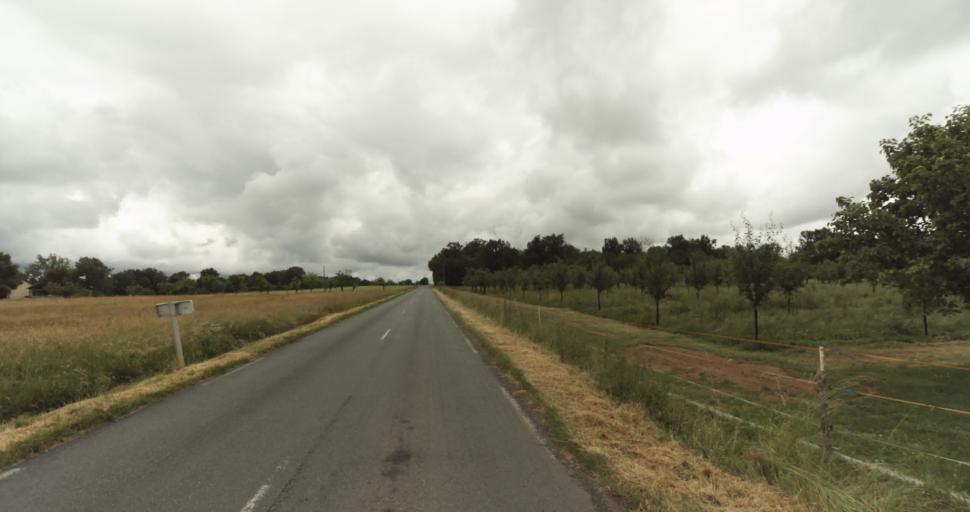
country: FR
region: Aquitaine
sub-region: Departement de la Dordogne
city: Beaumont-du-Perigord
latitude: 44.7422
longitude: 0.7813
